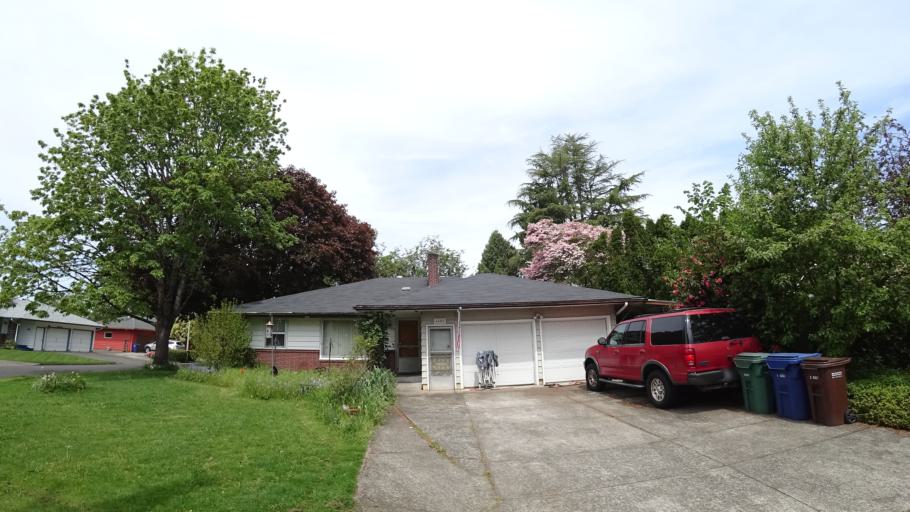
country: US
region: Oregon
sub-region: Clackamas County
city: Milwaukie
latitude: 45.4520
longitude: -122.6169
